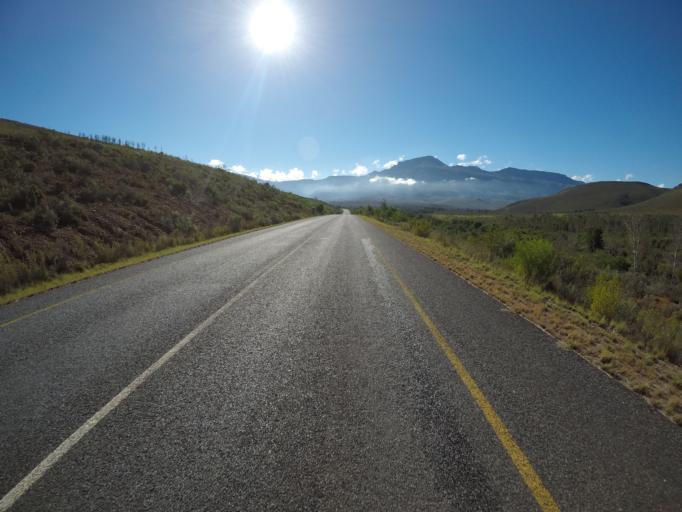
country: ZA
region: Western Cape
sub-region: Overberg District Municipality
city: Caledon
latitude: -34.0759
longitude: 19.5582
